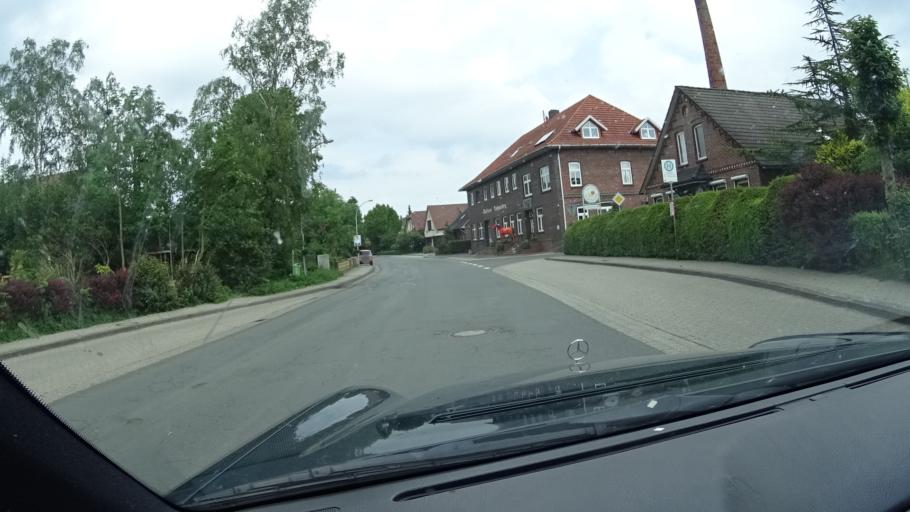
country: DE
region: Lower Saxony
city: Butjadingen
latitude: 53.5894
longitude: 8.2763
